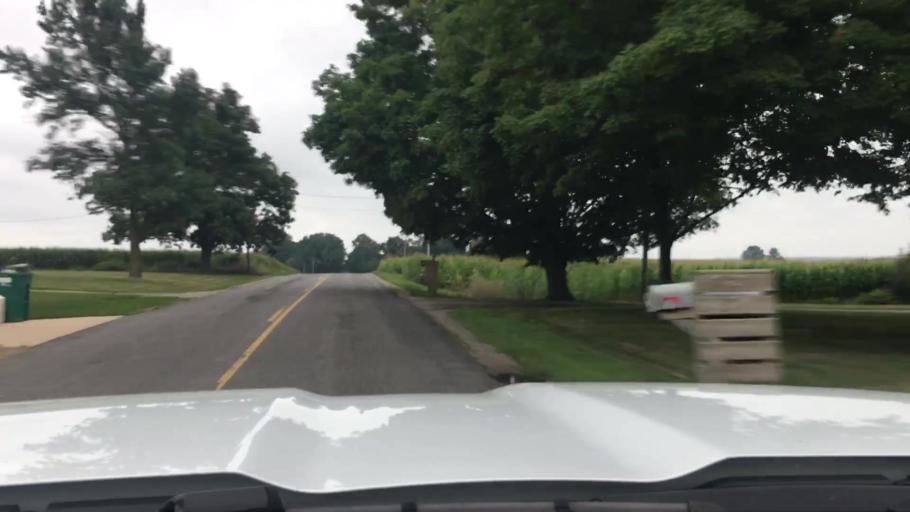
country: US
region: Michigan
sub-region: Ottawa County
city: Hudsonville
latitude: 42.7934
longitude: -85.8617
